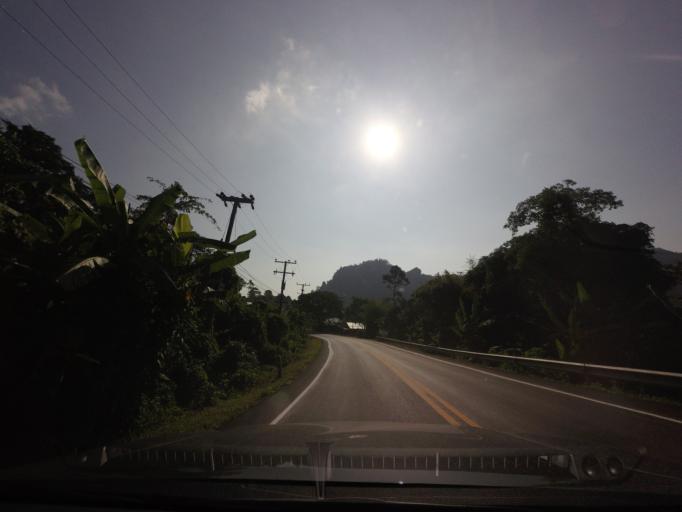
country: TH
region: Phetchabun
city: Lom Kao
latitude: 16.8687
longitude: 101.1364
